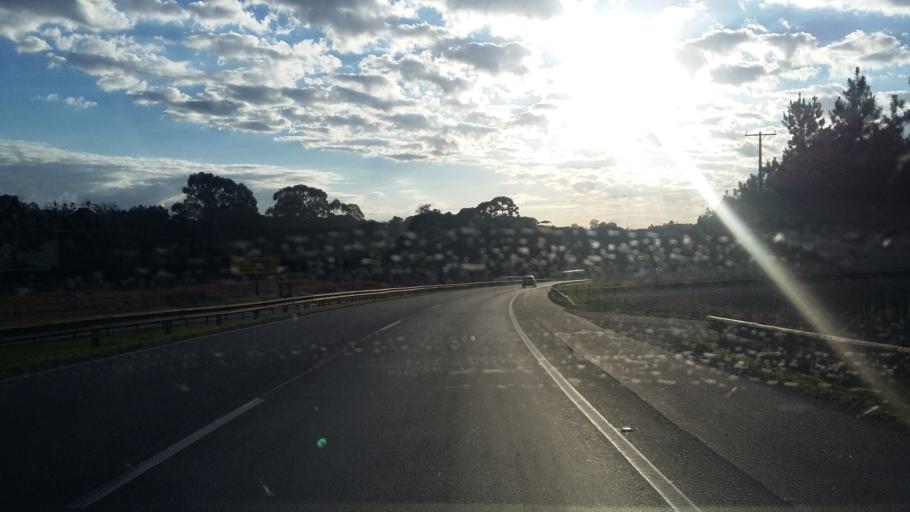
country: BR
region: Parana
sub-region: Curitiba
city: Curitiba
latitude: -25.4322
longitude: -49.3745
